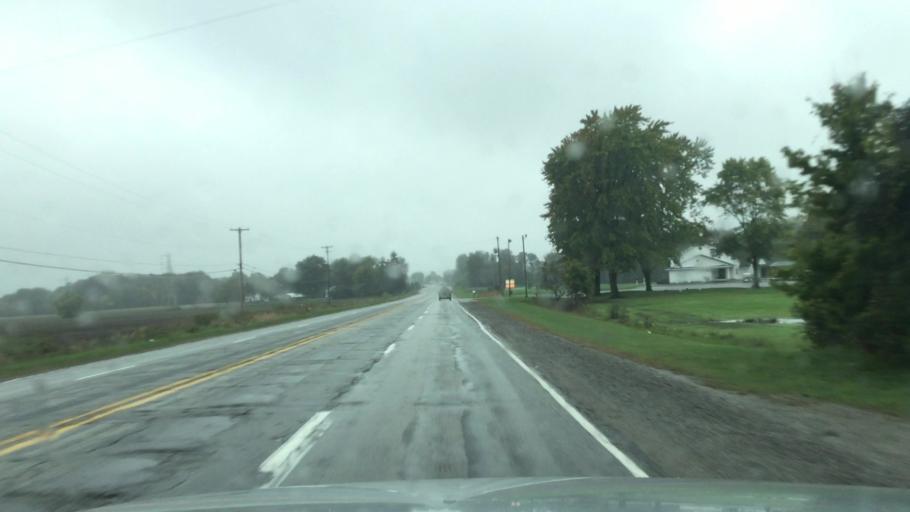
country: US
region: Michigan
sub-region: Saginaw County
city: Bridgeport
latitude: 43.3250
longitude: -83.8259
